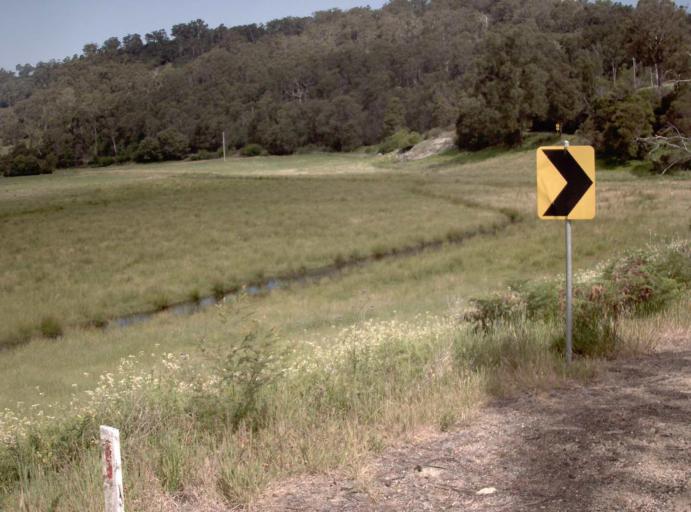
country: AU
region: New South Wales
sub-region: Bega Valley
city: Eden
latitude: -37.4794
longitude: 149.5988
